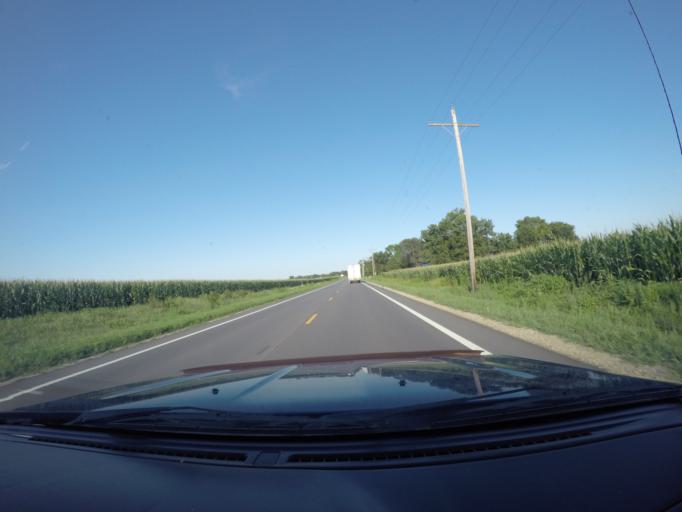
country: US
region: Kansas
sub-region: Douglas County
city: Lawrence
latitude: 39.0006
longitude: -95.2135
